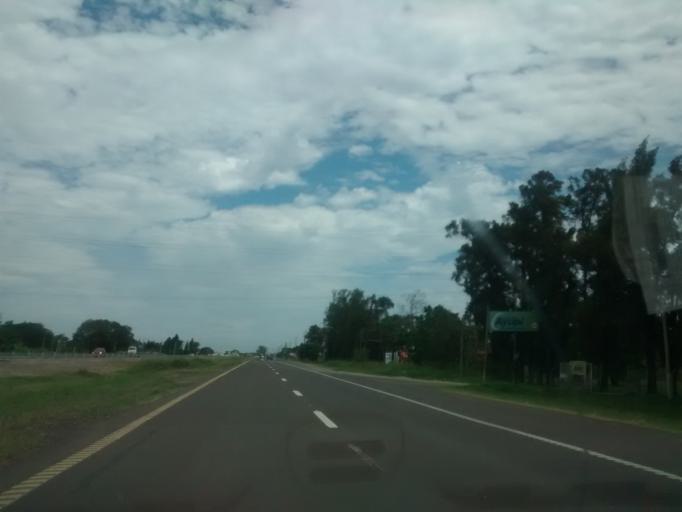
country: AR
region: Chaco
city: Fontana
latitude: -27.4052
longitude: -59.0101
